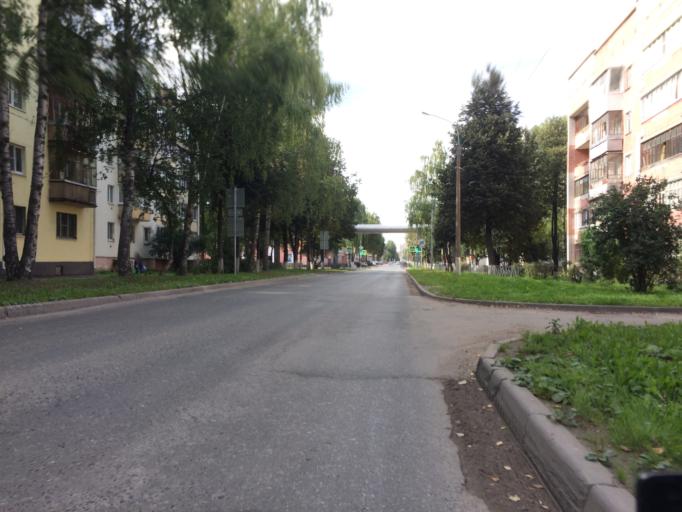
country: RU
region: Mariy-El
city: Yoshkar-Ola
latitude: 56.6309
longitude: 47.8772
